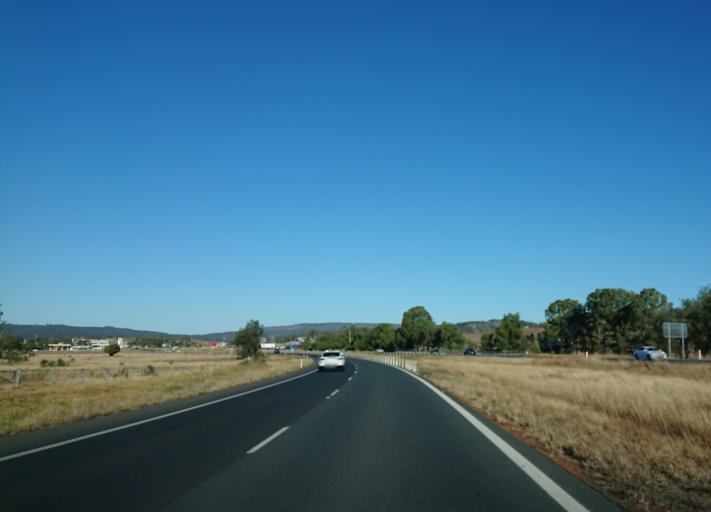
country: AU
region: Queensland
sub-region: Lockyer Valley
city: Gatton
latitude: -27.5638
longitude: 152.4436
